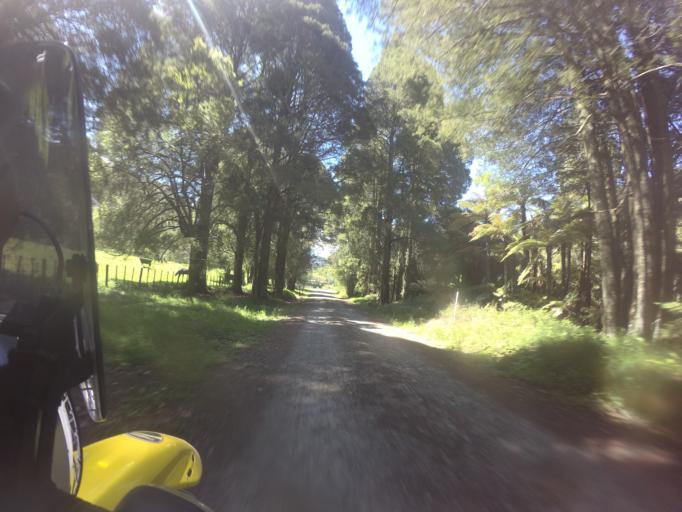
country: NZ
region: Bay of Plenty
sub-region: Opotiki District
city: Opotiki
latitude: -38.2948
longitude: 177.3378
